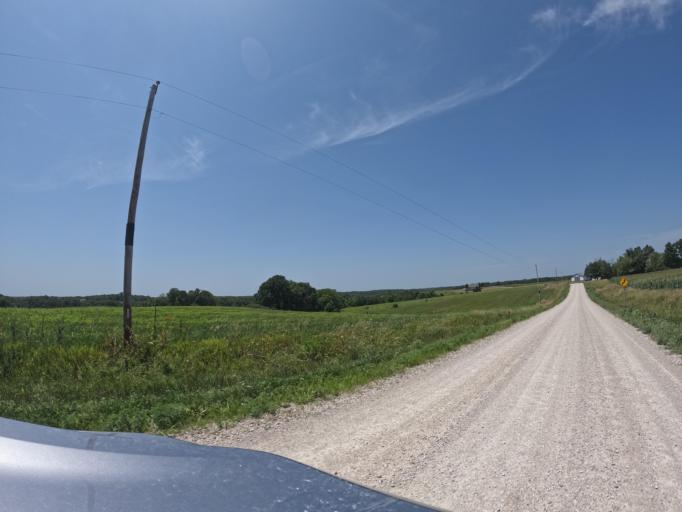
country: US
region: Iowa
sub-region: Henry County
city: Mount Pleasant
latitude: 40.9132
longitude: -91.6574
